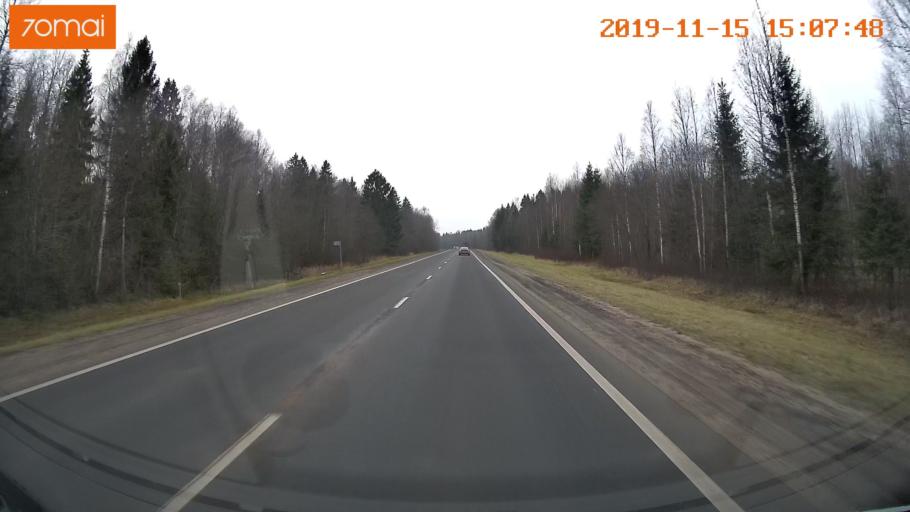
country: RU
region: Jaroslavl
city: Prechistoye
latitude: 58.3791
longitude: 40.2877
